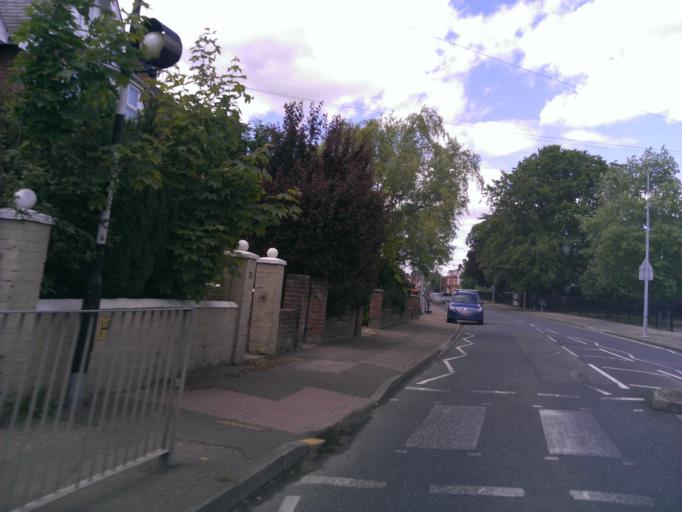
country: GB
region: England
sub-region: Essex
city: Colchester
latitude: 51.8792
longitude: 0.9164
